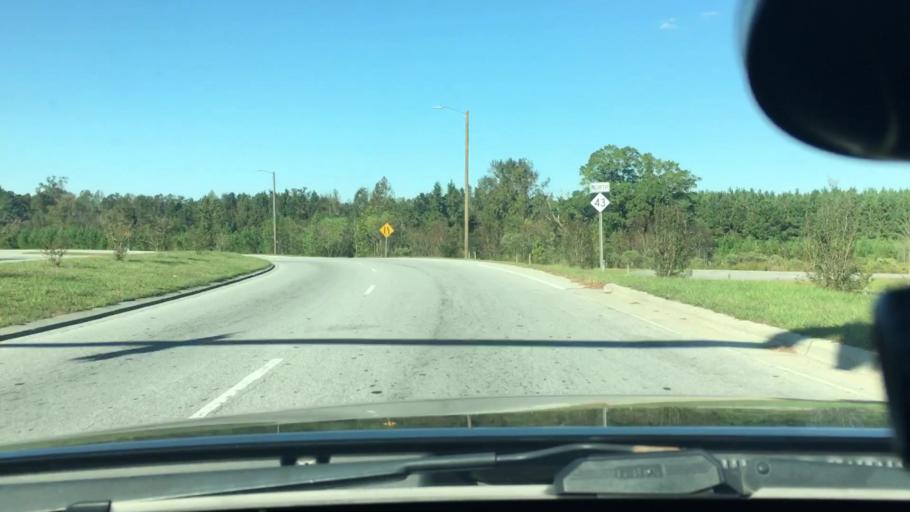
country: US
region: North Carolina
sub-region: Craven County
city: Trent Woods
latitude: 35.1443
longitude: -77.1062
